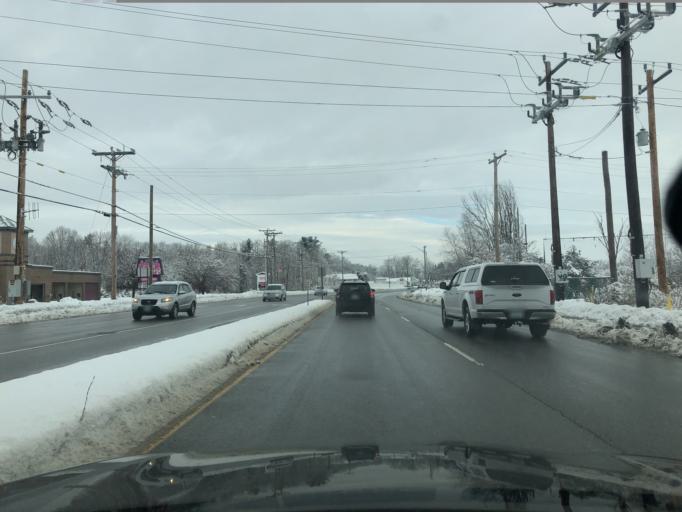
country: US
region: New Hampshire
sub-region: Strafford County
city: Somersworth
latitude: 43.2364
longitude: -70.8809
